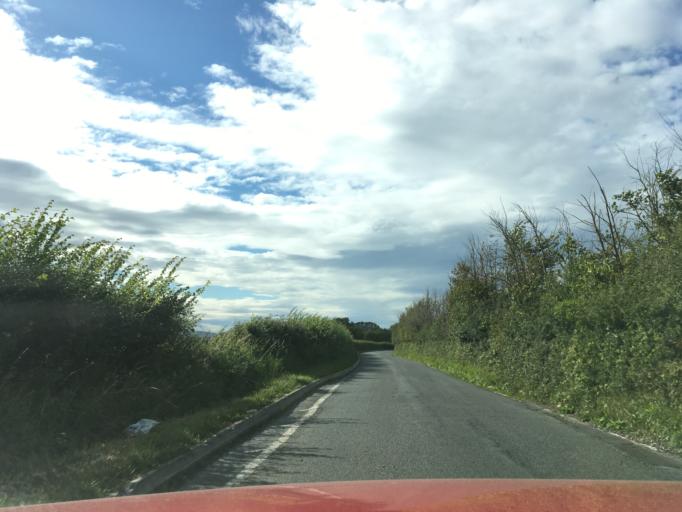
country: GB
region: England
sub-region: Gloucestershire
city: Gloucester
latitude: 51.8080
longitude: -2.2528
